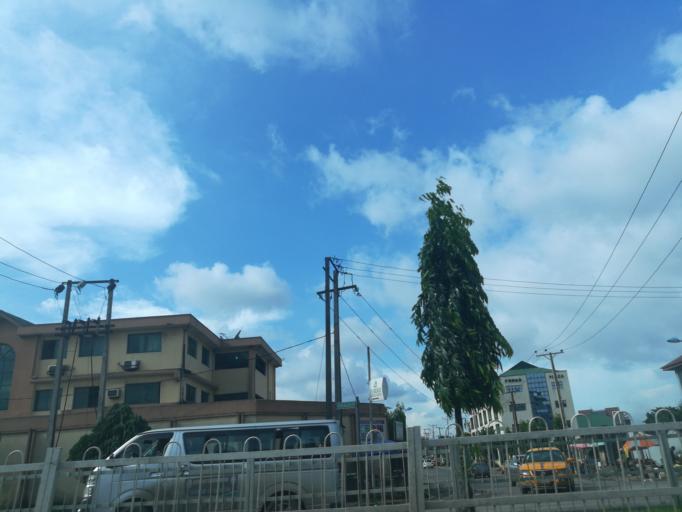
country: NG
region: Lagos
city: Ikeja
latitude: 6.6231
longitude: 3.3567
